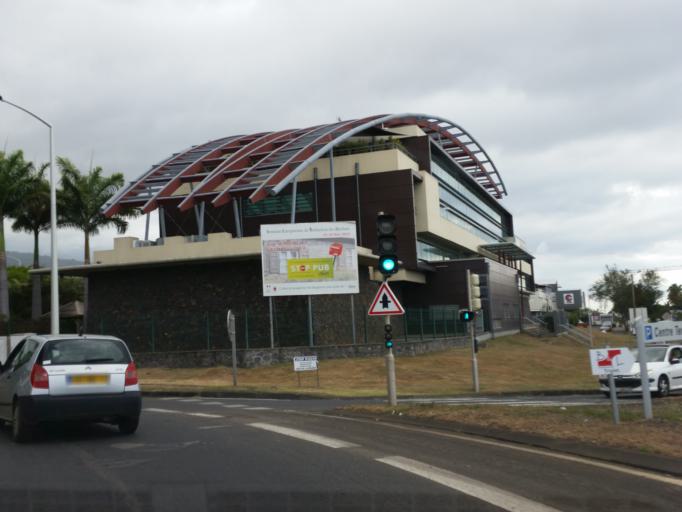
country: RE
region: Reunion
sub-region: Reunion
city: Sainte-Marie
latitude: -20.9021
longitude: 55.5028
